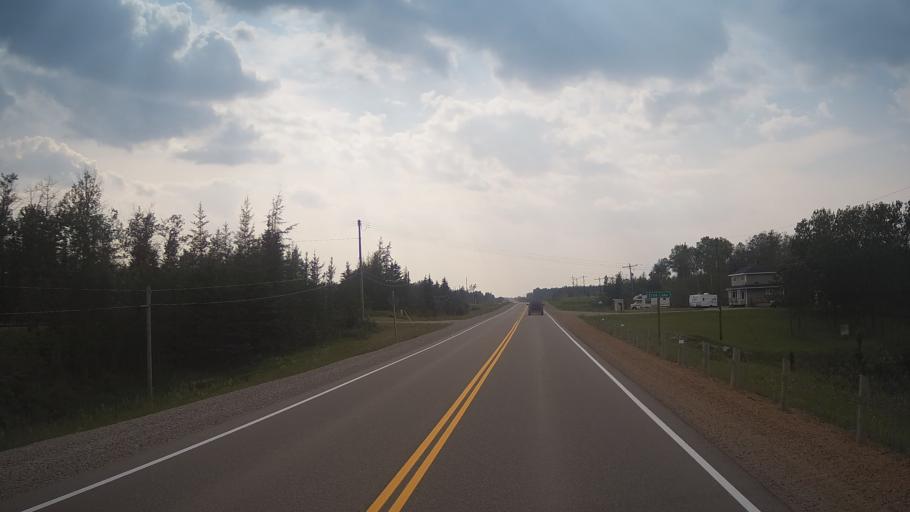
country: CA
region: Ontario
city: Kapuskasing
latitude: 49.4622
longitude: -82.6068
